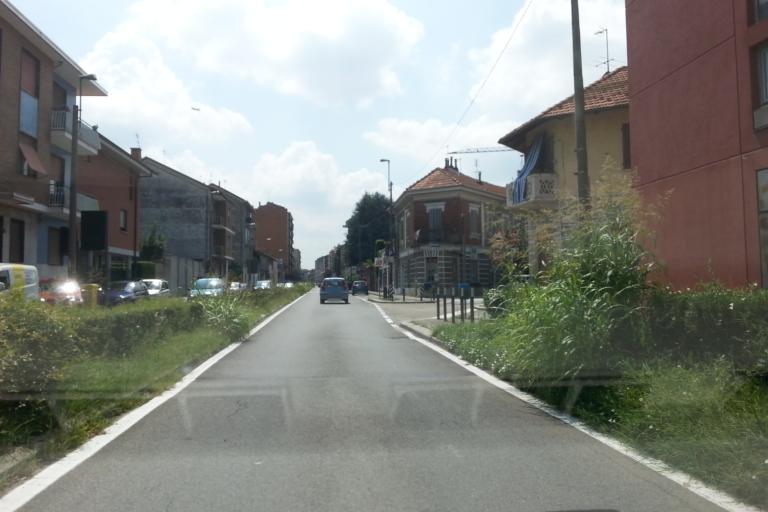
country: IT
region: Piedmont
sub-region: Provincia di Torino
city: Venaria Reale
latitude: 45.1327
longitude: 7.6331
